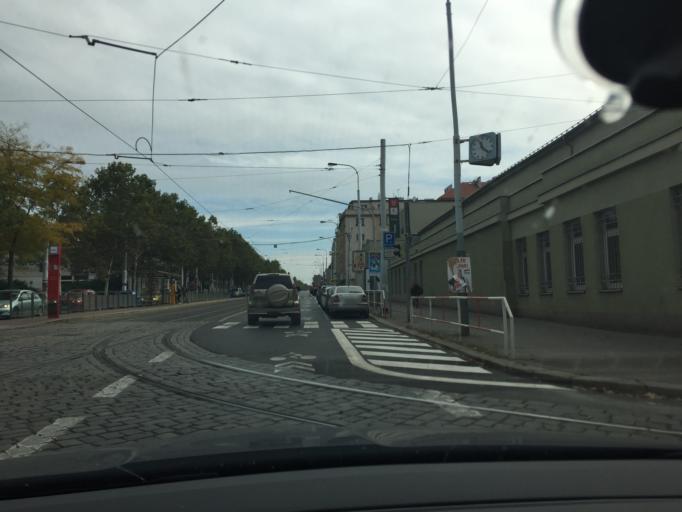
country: CZ
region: Praha
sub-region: Praha 8
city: Liben
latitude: 50.0915
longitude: 14.4749
